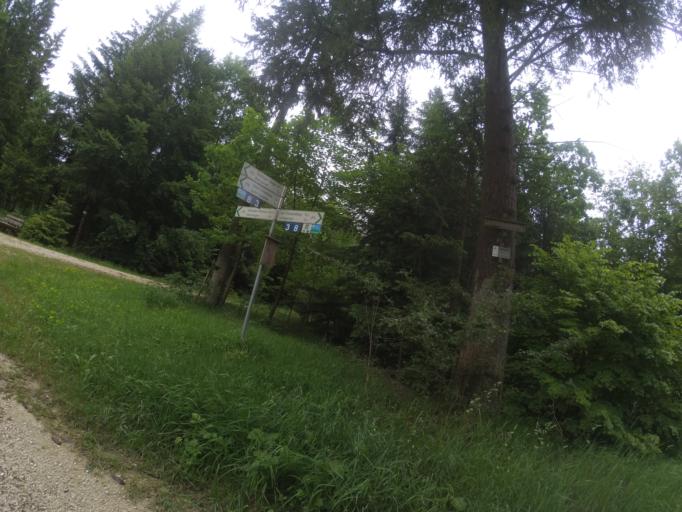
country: DE
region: Baden-Wuerttemberg
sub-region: Tuebingen Region
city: Borslingen
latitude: 48.5196
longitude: 10.0596
